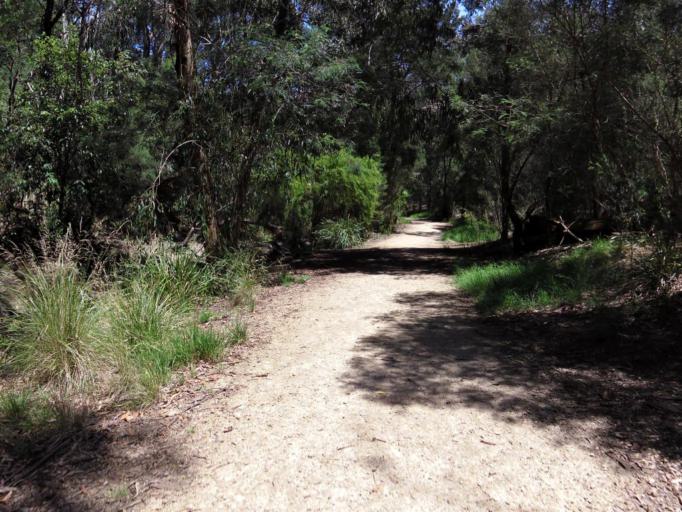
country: AU
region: Victoria
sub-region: Whitehorse
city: Burwood
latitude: -37.8656
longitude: 145.1260
